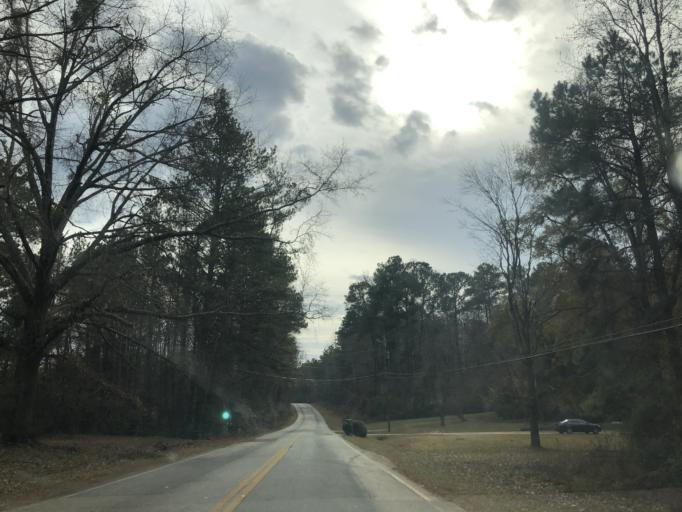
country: US
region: Georgia
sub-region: DeKalb County
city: Pine Mountain
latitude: 33.6693
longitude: -84.1798
